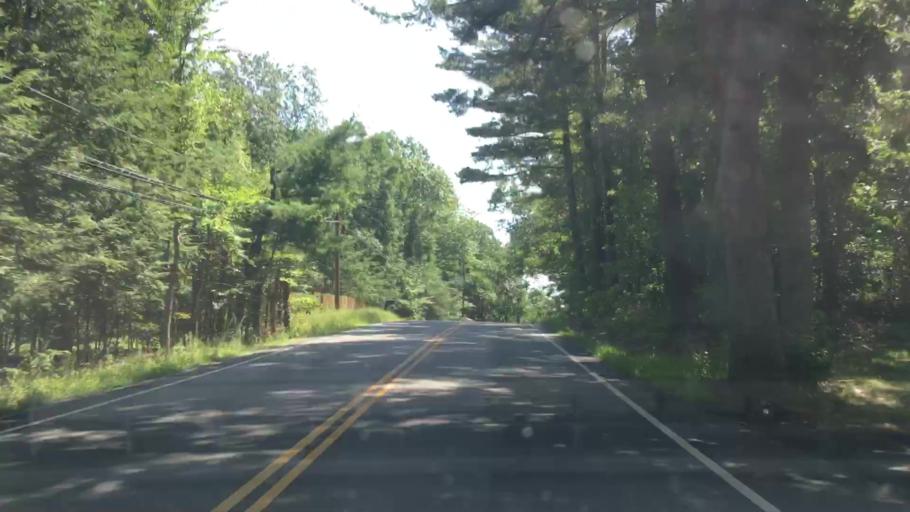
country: US
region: New Hampshire
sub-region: Rockingham County
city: Hampstead
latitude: 42.8562
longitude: -71.2195
